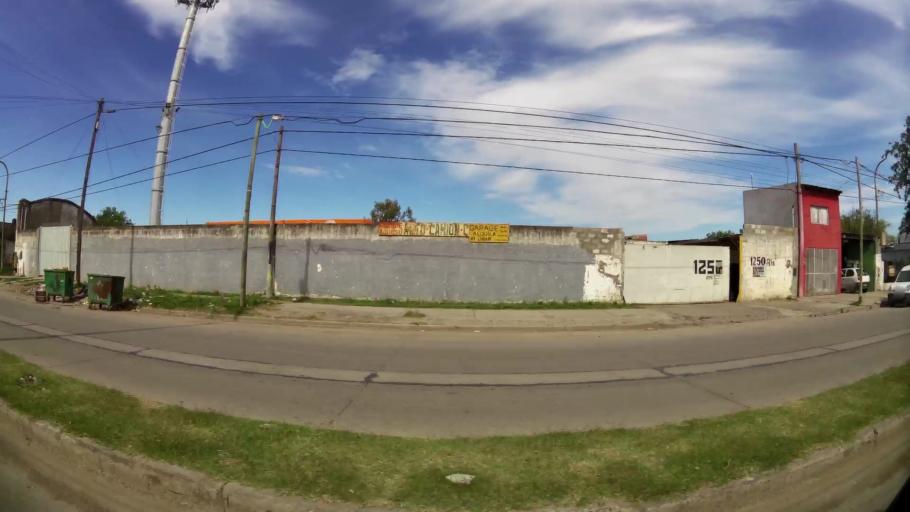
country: AR
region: Santa Fe
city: Granadero Baigorria
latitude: -32.9144
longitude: -60.7139
